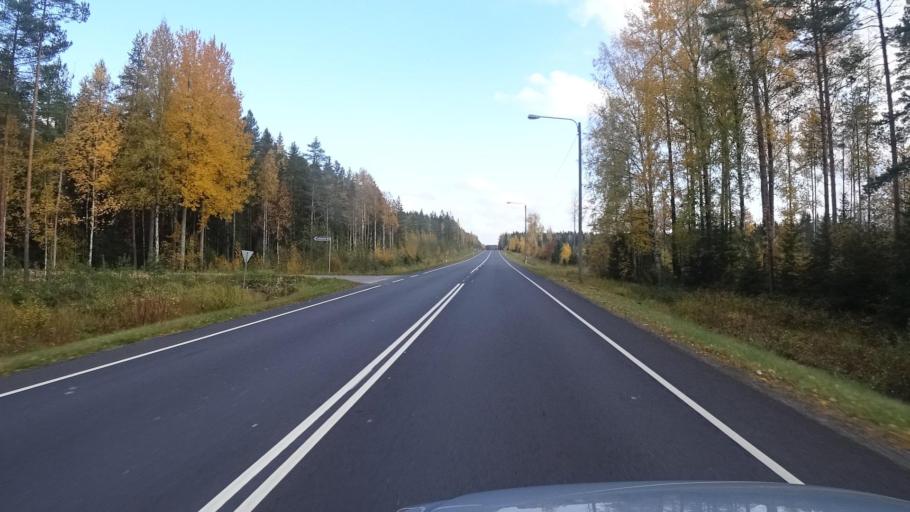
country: FI
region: Satakunta
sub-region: Rauma
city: Eura
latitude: 61.1163
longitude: 22.1925
